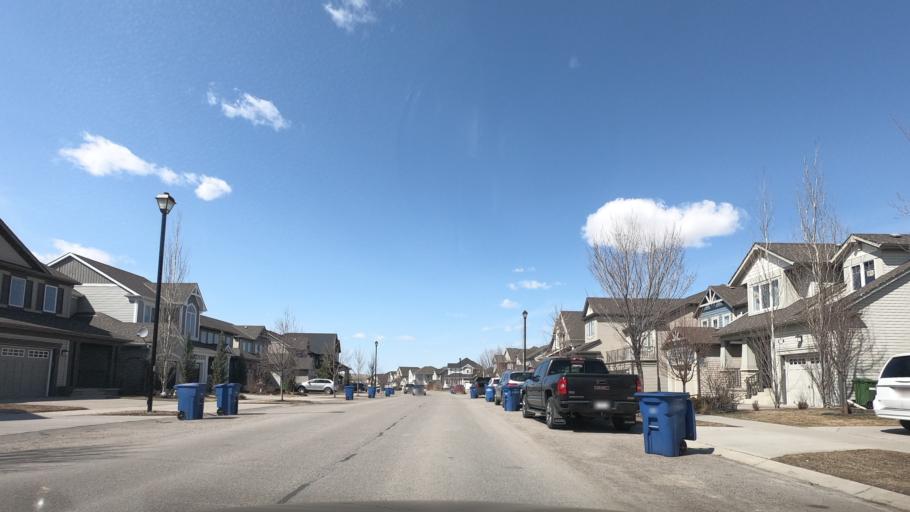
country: CA
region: Alberta
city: Airdrie
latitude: 51.2620
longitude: -114.0300
